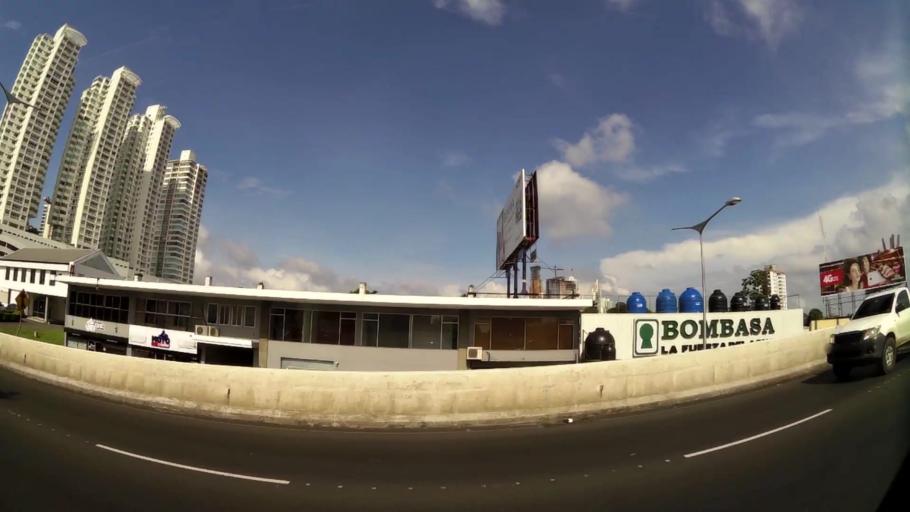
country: PA
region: Panama
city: Panama
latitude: 8.9953
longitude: -79.5282
